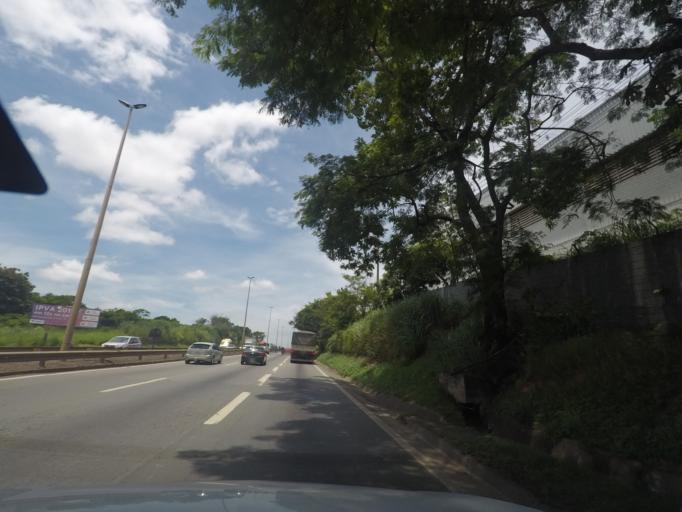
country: BR
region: Goias
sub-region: Goiania
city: Goiania
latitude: -16.6858
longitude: -49.2337
